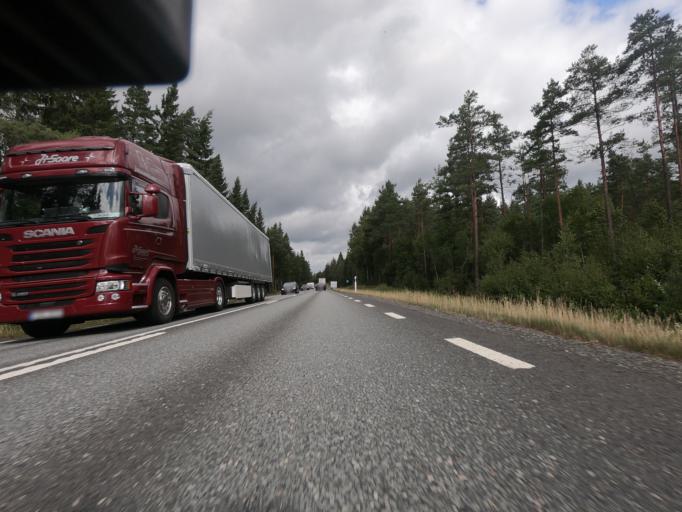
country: SE
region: Joenkoeping
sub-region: Savsjo Kommun
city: Vrigstad
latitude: 57.3949
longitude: 14.3791
